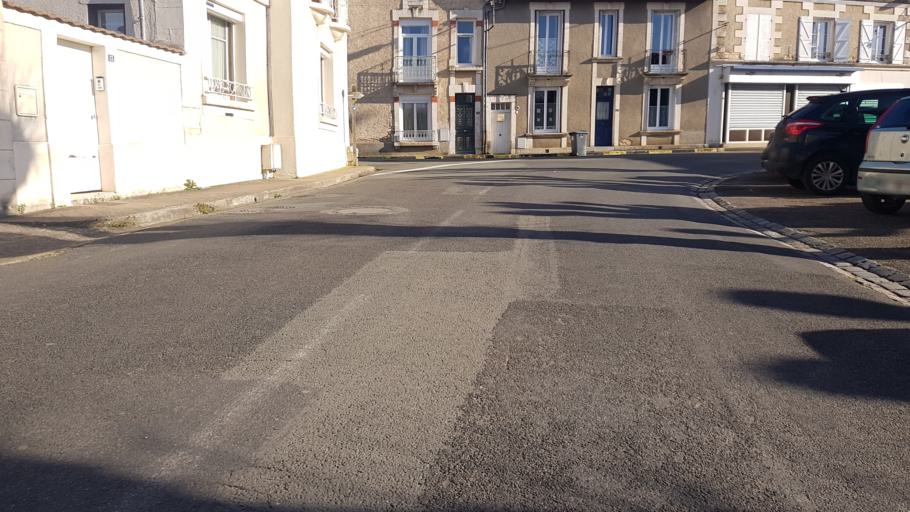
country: FR
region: Poitou-Charentes
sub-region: Departement de la Vienne
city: Migne-Auxances
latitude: 46.6268
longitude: 0.3116
